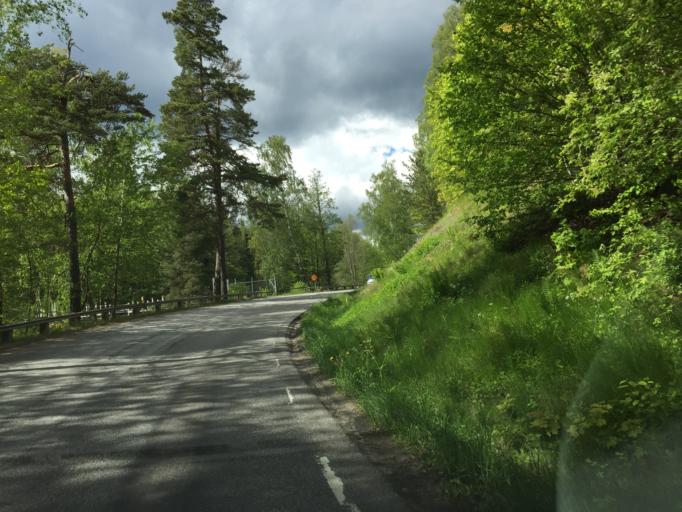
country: SE
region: OEstergoetland
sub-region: Finspangs Kommun
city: Finspang
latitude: 58.7173
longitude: 15.8333
